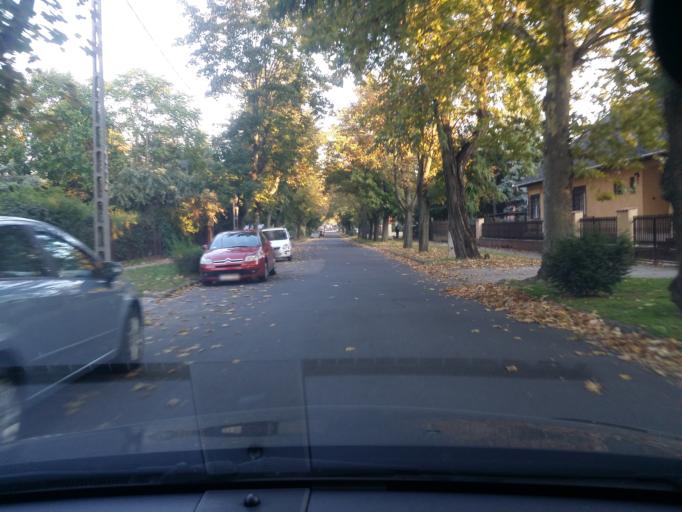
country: HU
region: Budapest
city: Budapest XV. keruelet
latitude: 47.5668
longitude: 19.1074
